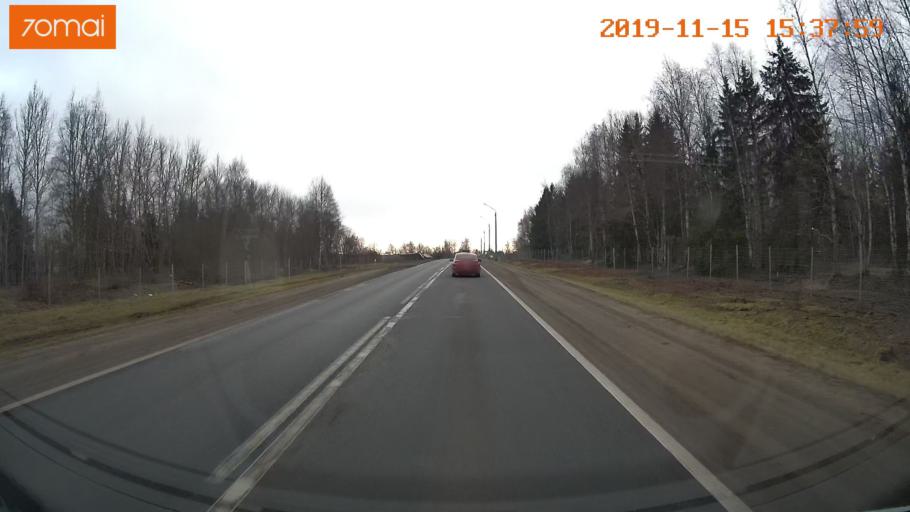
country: RU
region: Jaroslavl
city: Danilov
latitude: 58.0340
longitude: 40.0848
